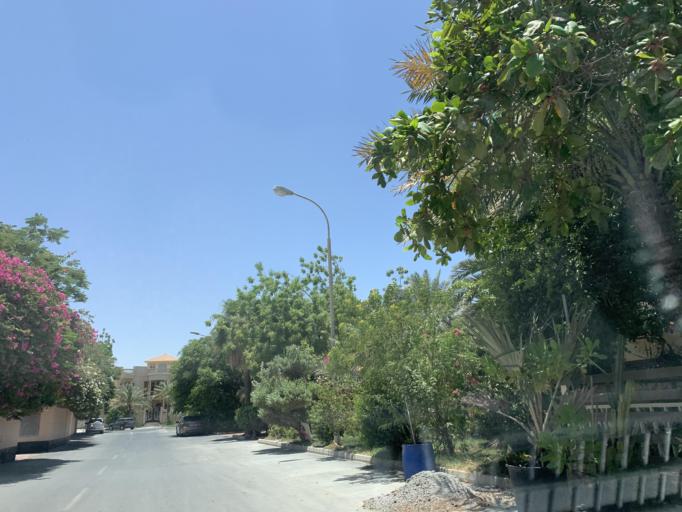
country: BH
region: Manama
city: Jidd Hafs
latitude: 26.2288
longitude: 50.4855
